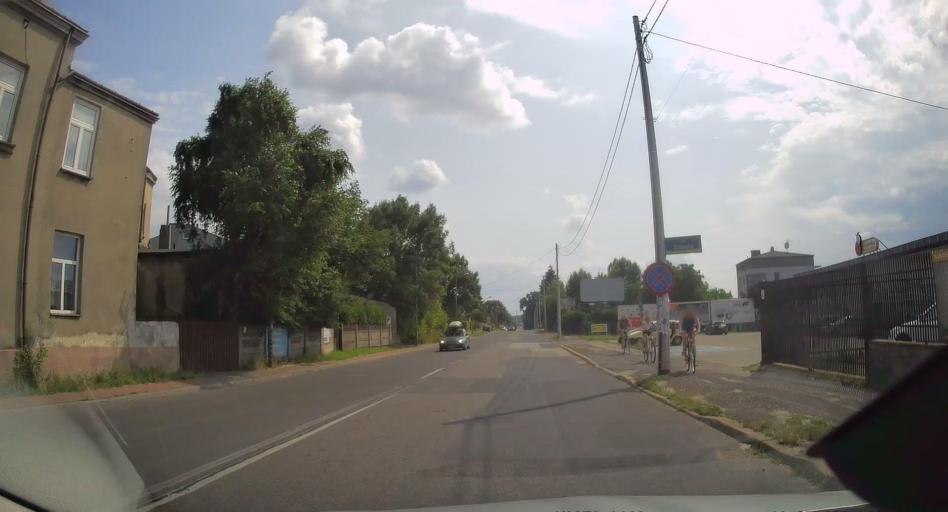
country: PL
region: Silesian Voivodeship
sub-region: Czestochowa
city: Czestochowa
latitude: 50.8124
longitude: 19.0837
